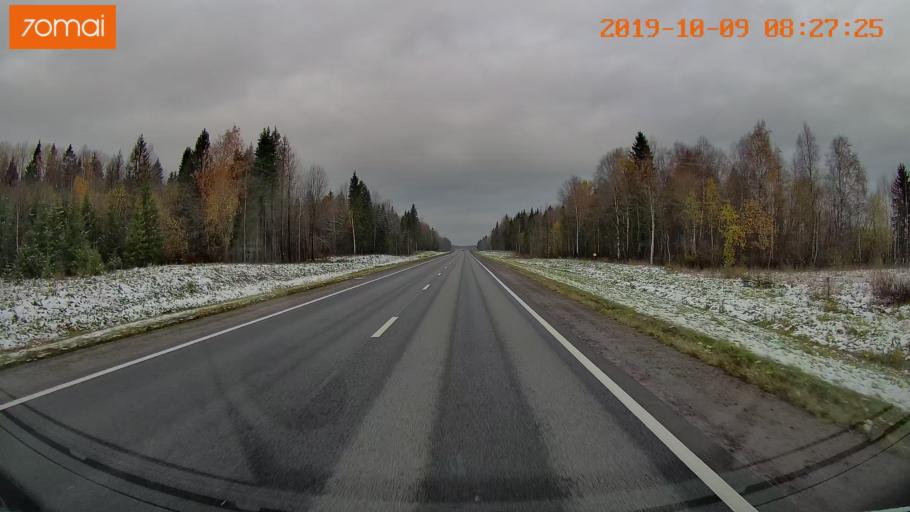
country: RU
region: Vologda
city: Gryazovets
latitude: 58.8037
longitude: 40.2488
